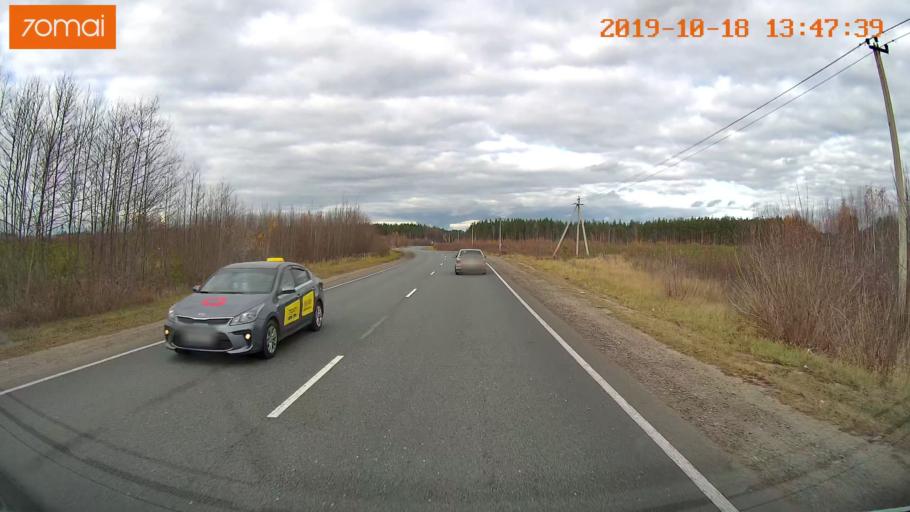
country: RU
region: Moskovskaya
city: Radovitskiy
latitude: 54.9781
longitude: 39.9515
